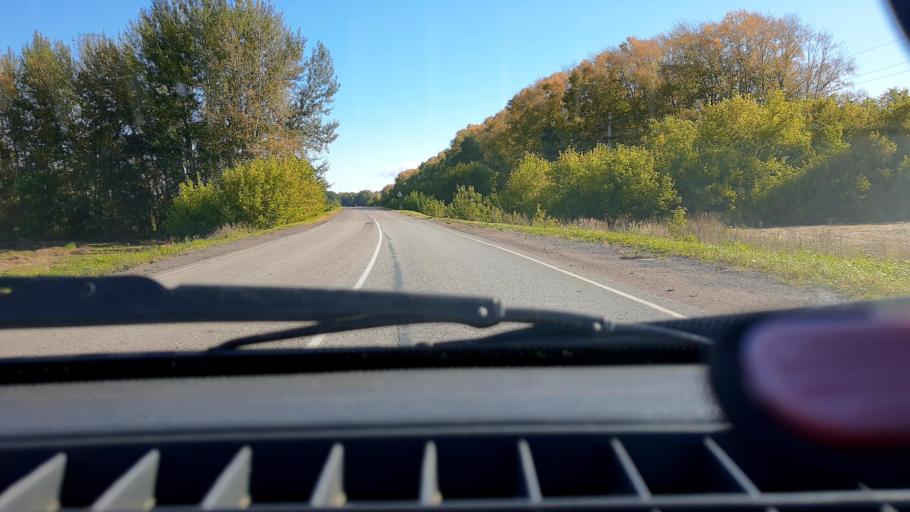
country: RU
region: Bashkortostan
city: Kushnarenkovo
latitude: 55.0599
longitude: 55.4331
